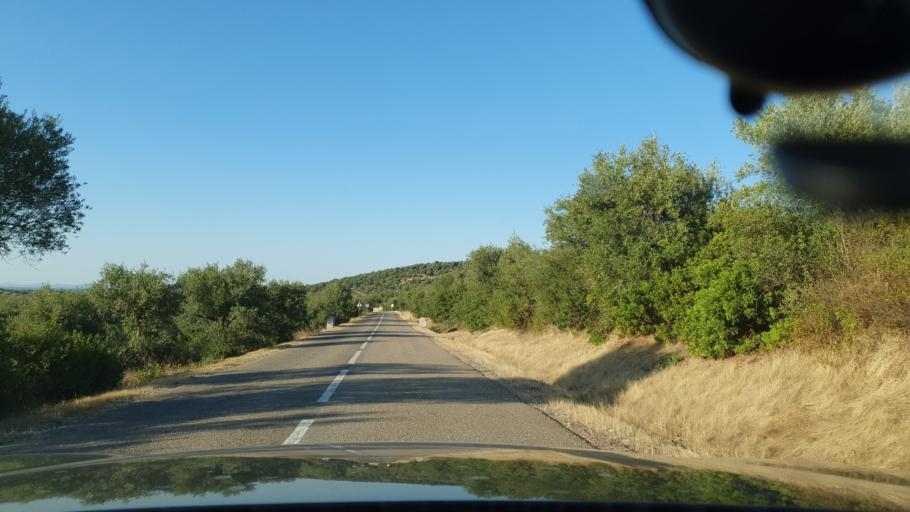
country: PT
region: Evora
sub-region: Estremoz
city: Estremoz
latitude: 38.9236
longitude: -7.6665
